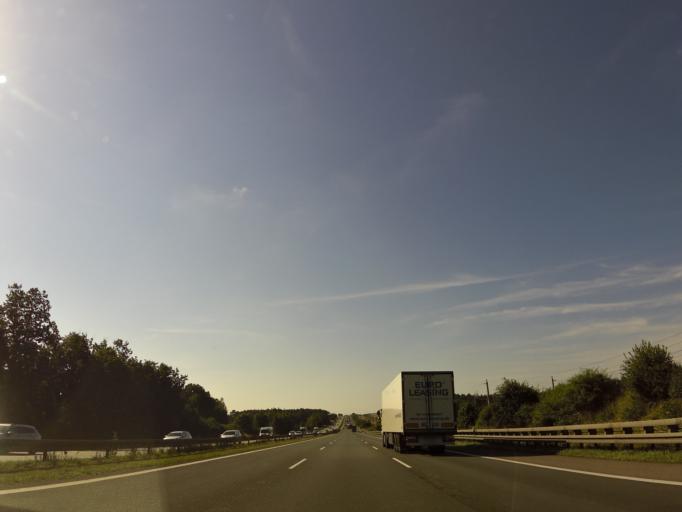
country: DE
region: Bavaria
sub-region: Regierungsbezirk Mittelfranken
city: Hilpoltstein
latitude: 49.1949
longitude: 11.2449
